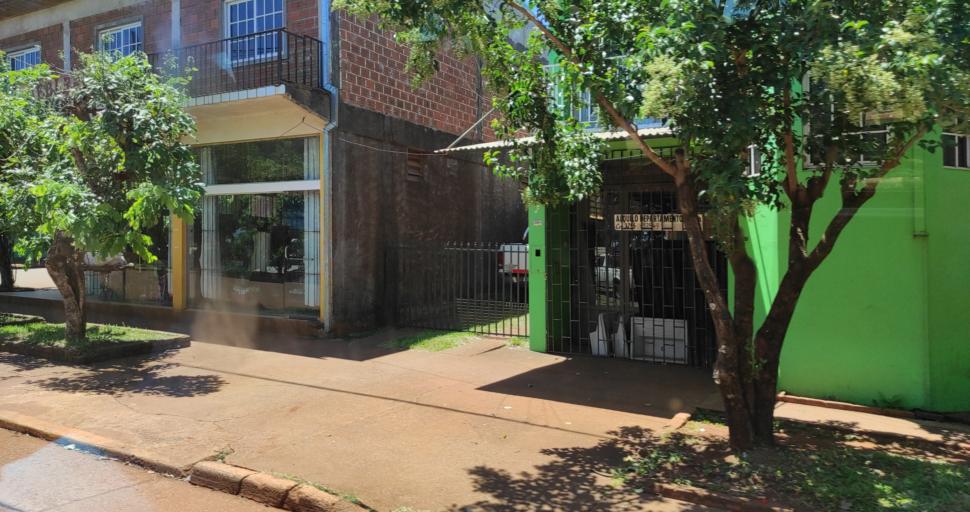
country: AR
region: Misiones
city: Dos de Mayo
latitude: -26.9915
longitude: -54.4789
